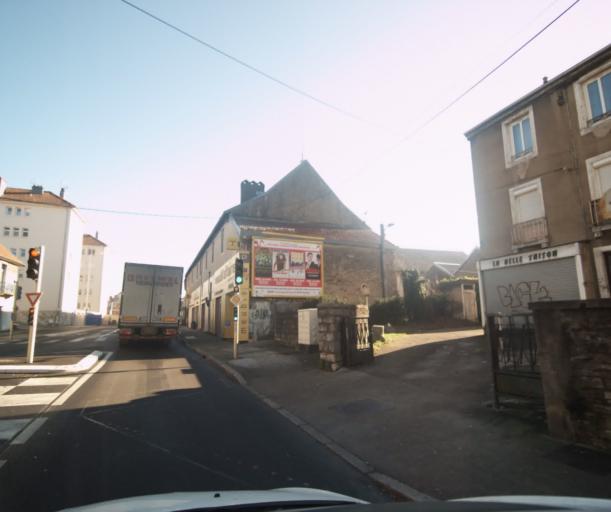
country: FR
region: Franche-Comte
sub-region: Departement du Doubs
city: Besancon
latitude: 47.2341
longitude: 6.0082
